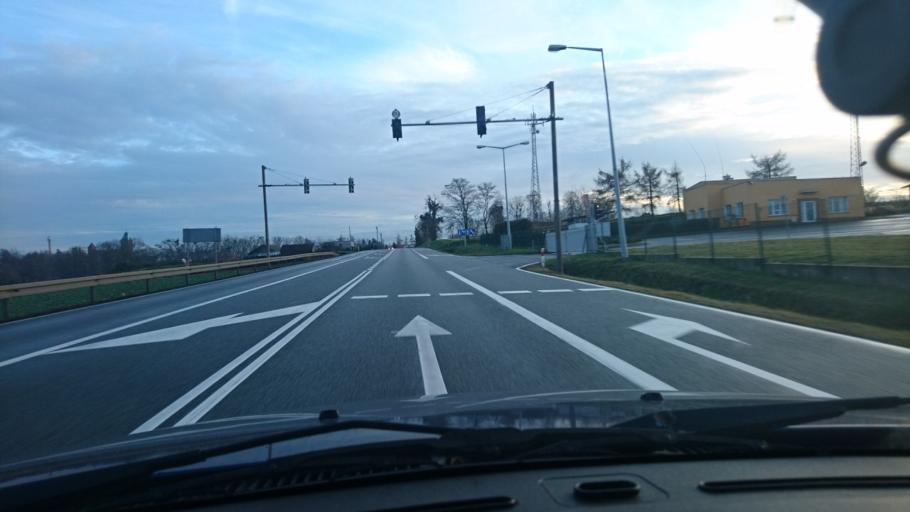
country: PL
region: Opole Voivodeship
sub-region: Powiat kluczborski
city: Byczyna
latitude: 51.1193
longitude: 18.2074
